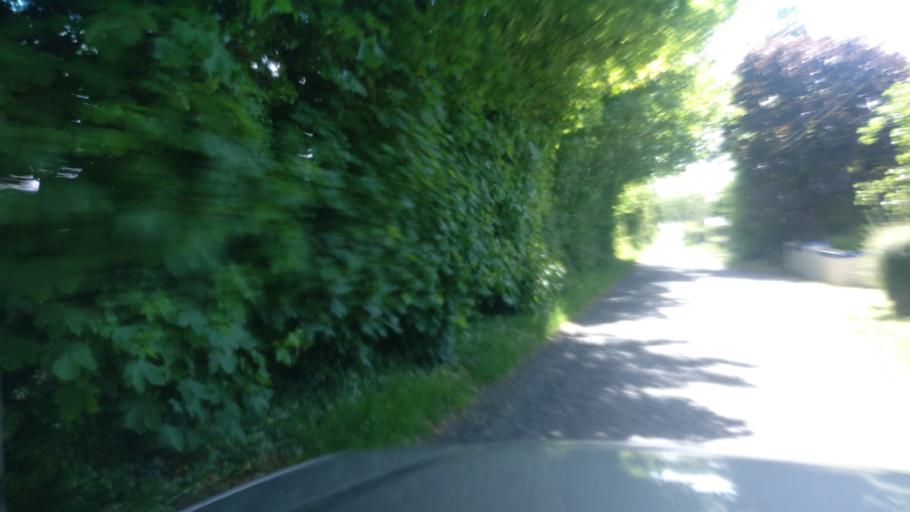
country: IE
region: Connaught
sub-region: County Galway
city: Gort
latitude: 53.1503
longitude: -8.7468
